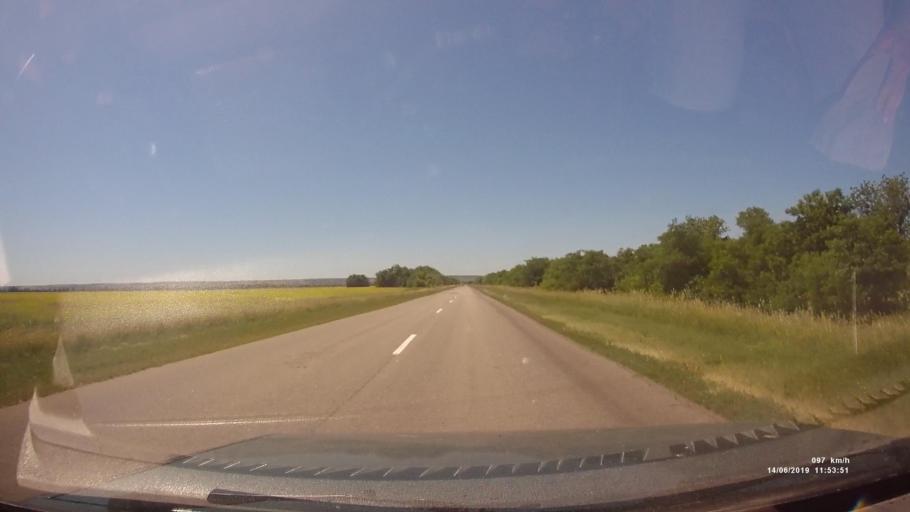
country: RU
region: Rostov
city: Kazanskaya
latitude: 49.8239
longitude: 41.2048
